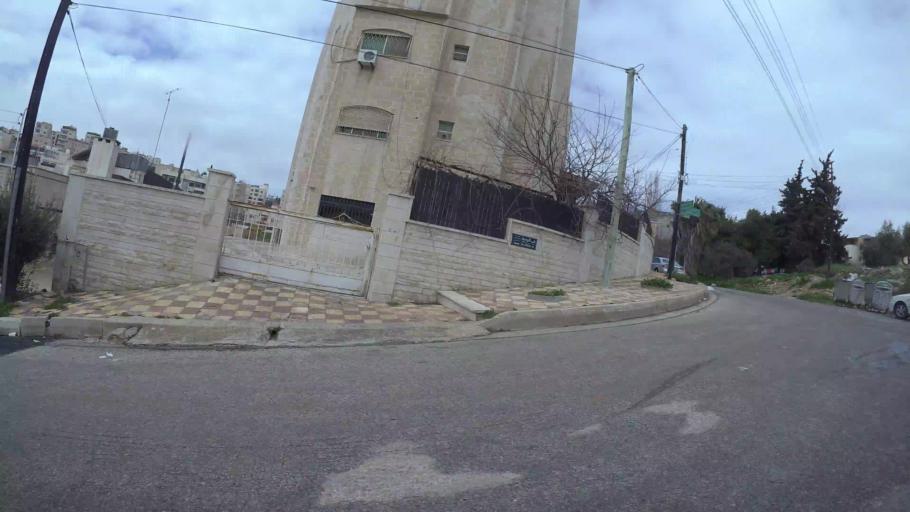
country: JO
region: Amman
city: Al Jubayhah
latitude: 31.9920
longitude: 35.8575
